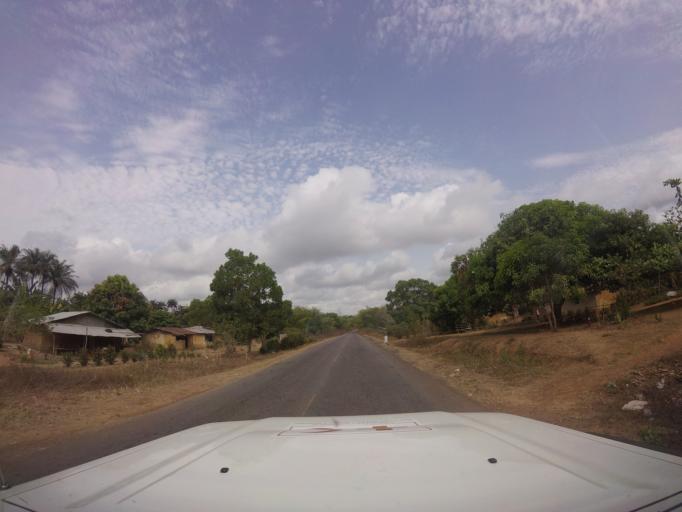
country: LR
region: Bomi
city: Tubmanburg
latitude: 6.6968
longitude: -10.9062
